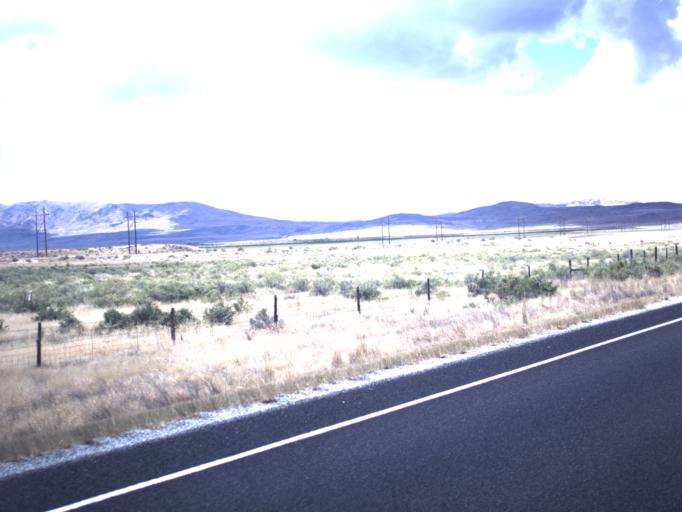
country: US
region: Utah
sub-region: Box Elder County
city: Tremonton
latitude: 41.6211
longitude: -112.3875
